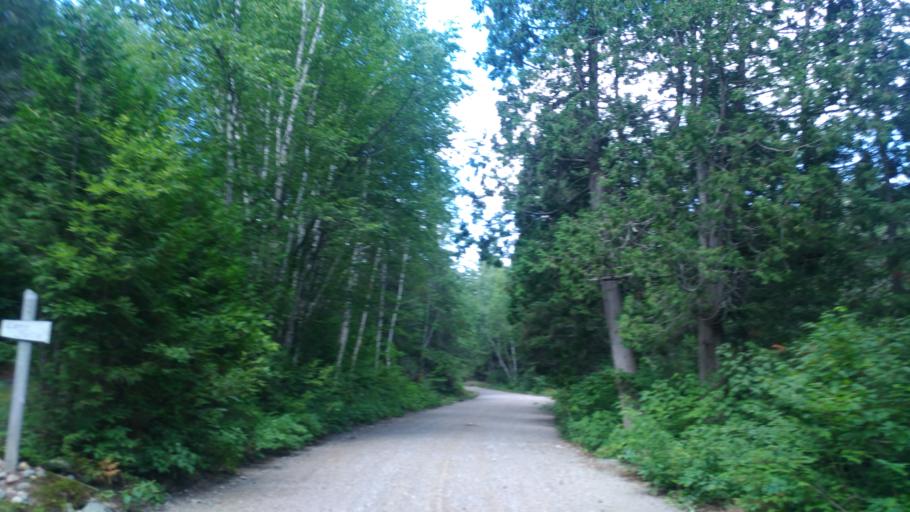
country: CA
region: Ontario
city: Rayside-Balfour
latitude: 46.5897
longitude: -81.5475
